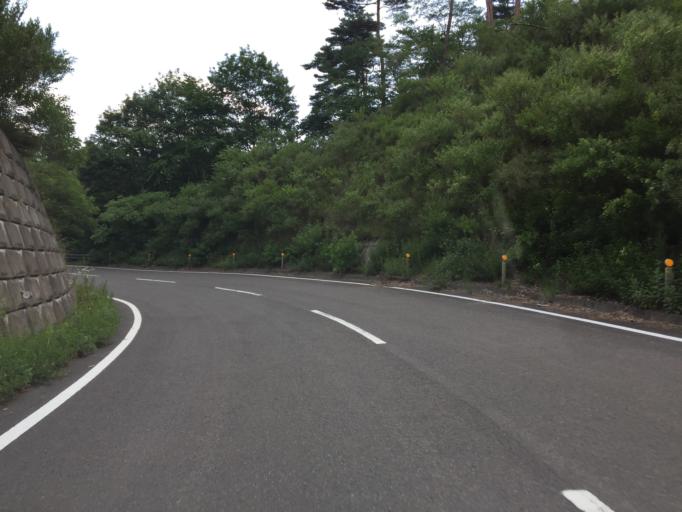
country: JP
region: Fukushima
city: Yanagawamachi-saiwaicho
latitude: 37.7678
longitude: 140.6737
